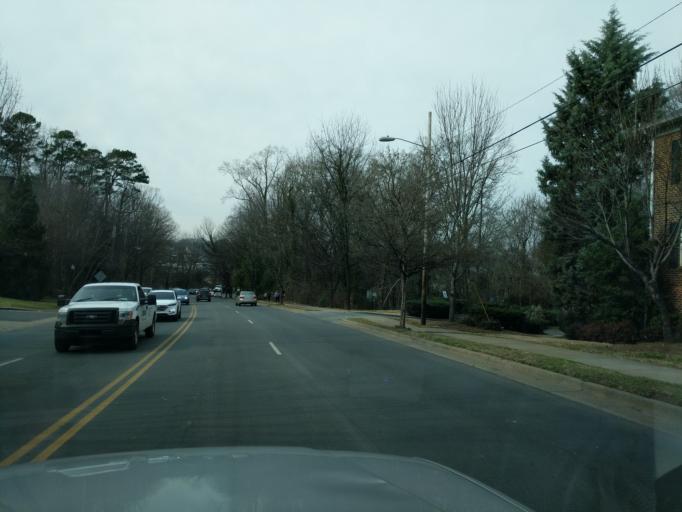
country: US
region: North Carolina
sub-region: Mecklenburg County
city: Charlotte
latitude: 35.1711
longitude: -80.8421
